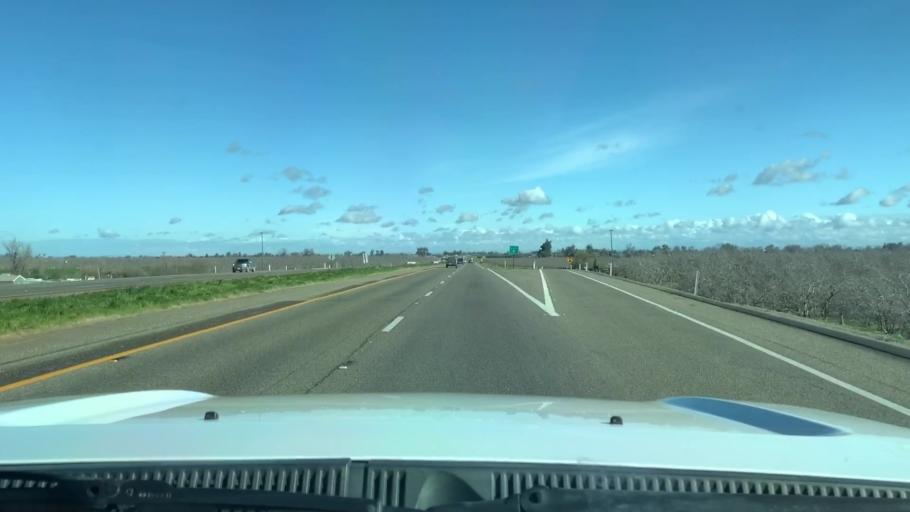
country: US
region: California
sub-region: Fresno County
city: Riverdale
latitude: 36.3987
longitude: -119.8075
